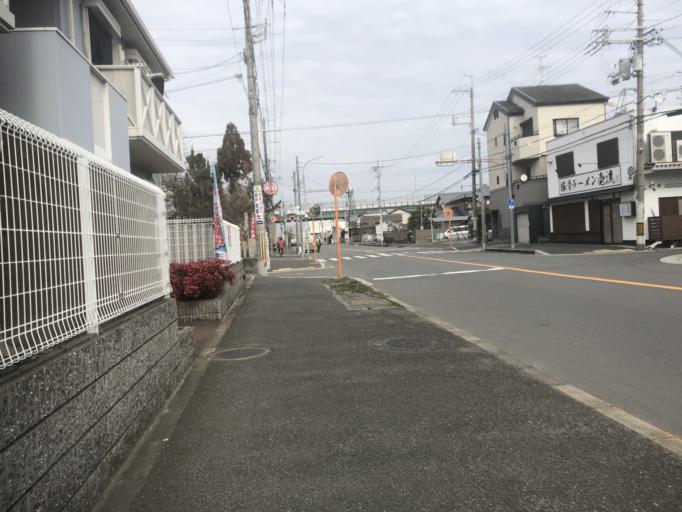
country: JP
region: Osaka
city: Daitocho
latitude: 34.6772
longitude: 135.5788
